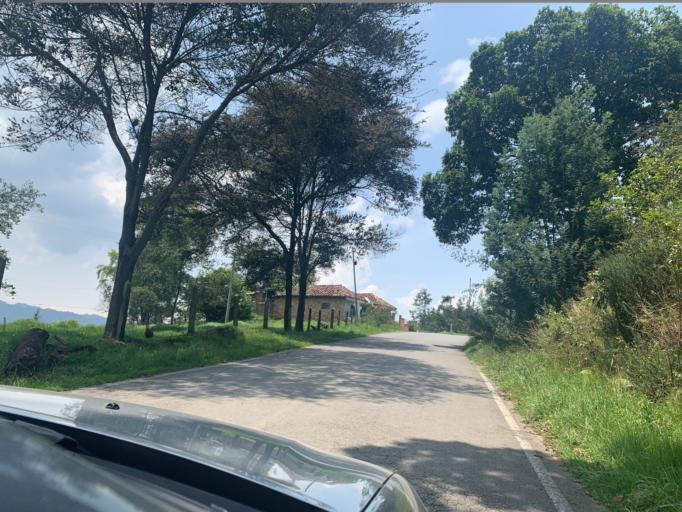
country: CO
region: Boyaca
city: Chiquinquira
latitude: 5.5772
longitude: -73.7480
